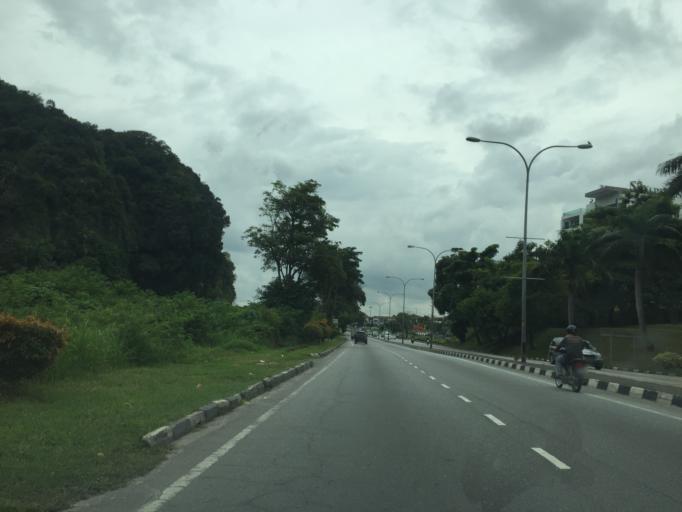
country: MY
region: Perak
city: Ipoh
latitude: 4.5632
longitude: 101.1130
